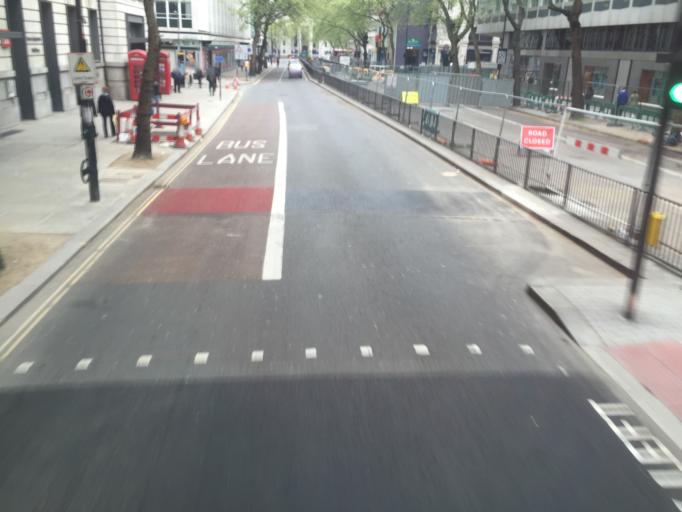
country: GB
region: England
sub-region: Greater London
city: London
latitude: 51.5154
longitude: -0.1190
